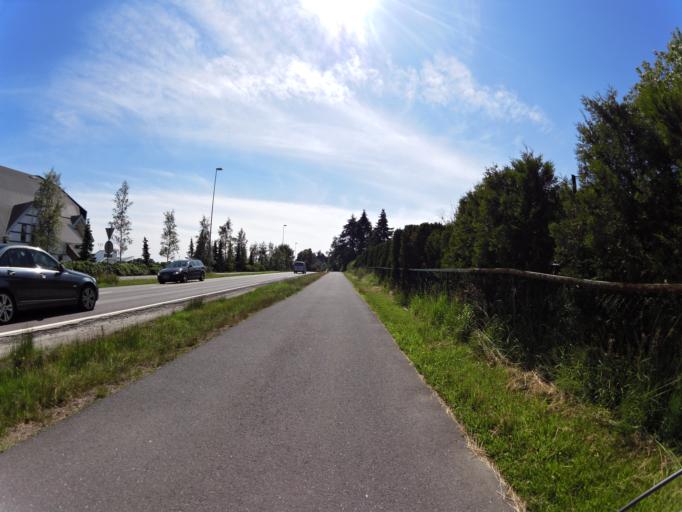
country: NO
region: Ostfold
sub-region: Fredrikstad
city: Fredrikstad
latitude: 59.2522
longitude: 10.9917
